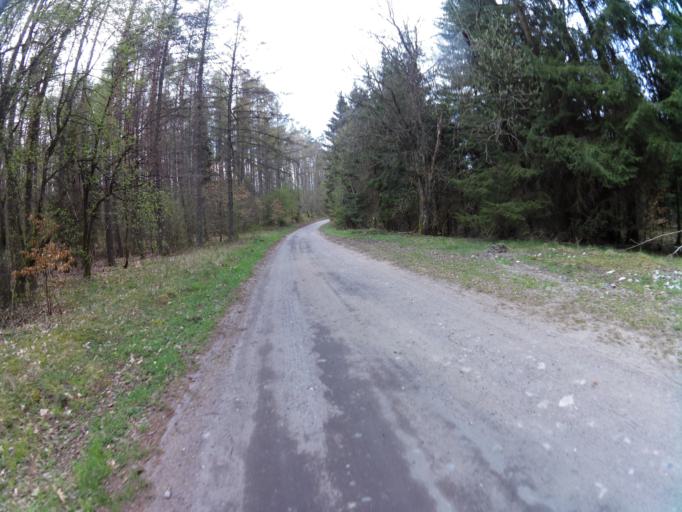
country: PL
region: West Pomeranian Voivodeship
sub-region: Powiat koszalinski
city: Bobolice
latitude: 53.8572
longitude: 16.6837
